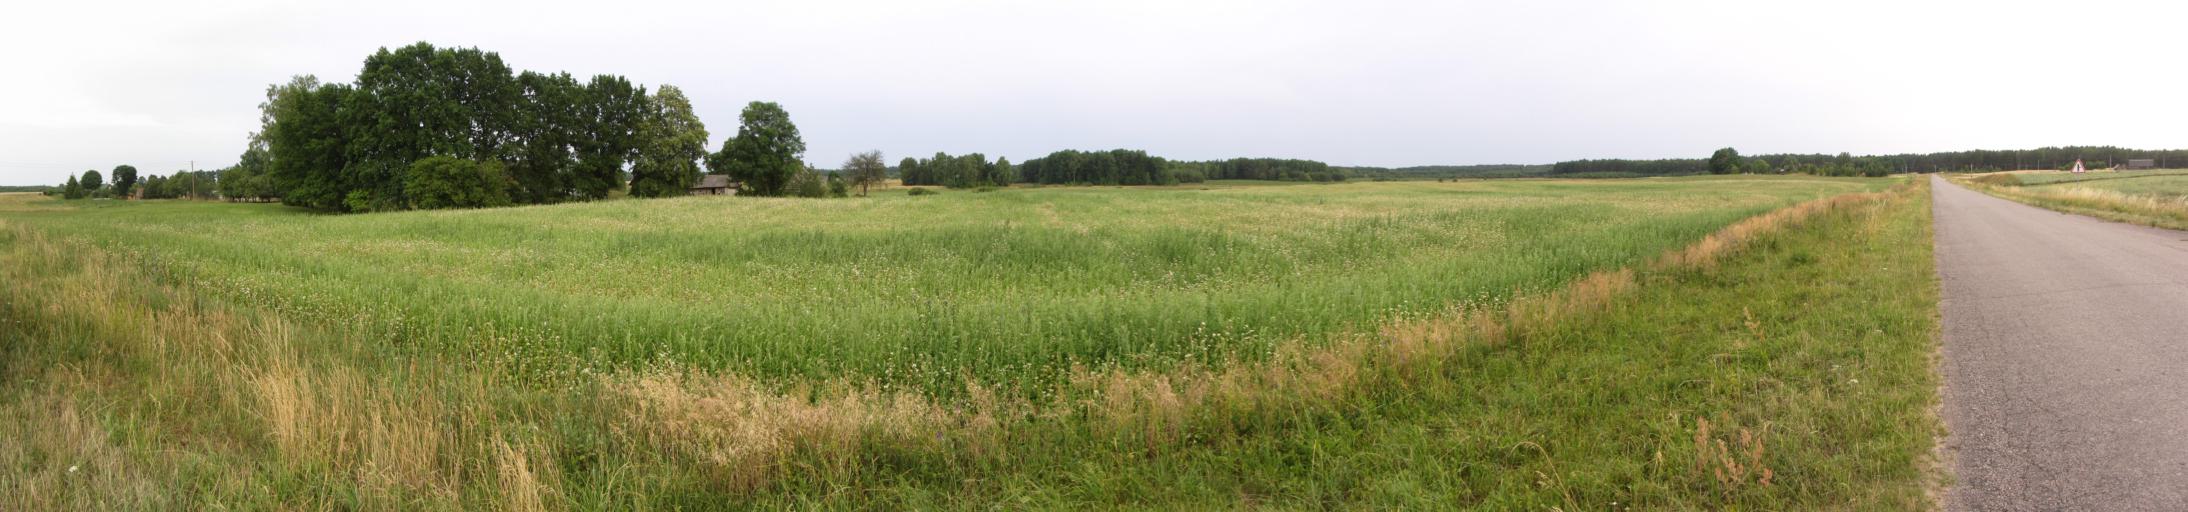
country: LT
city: Veisiejai
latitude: 54.0211
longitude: 23.7368
